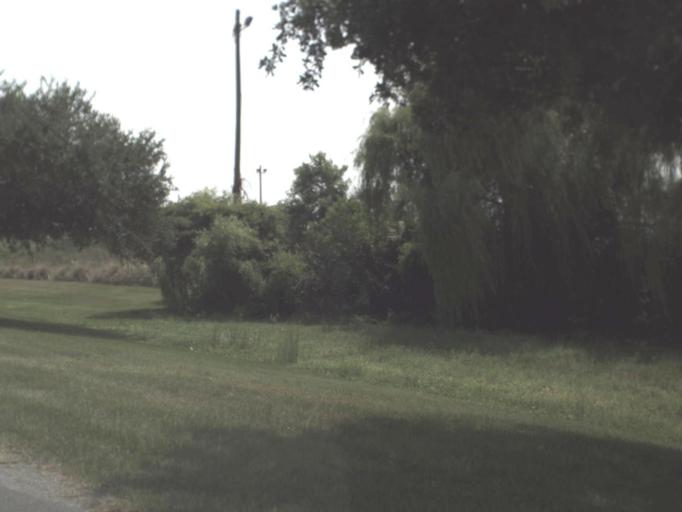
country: US
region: Florida
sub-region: Duval County
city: Jacksonville
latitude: 30.4073
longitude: -81.5371
